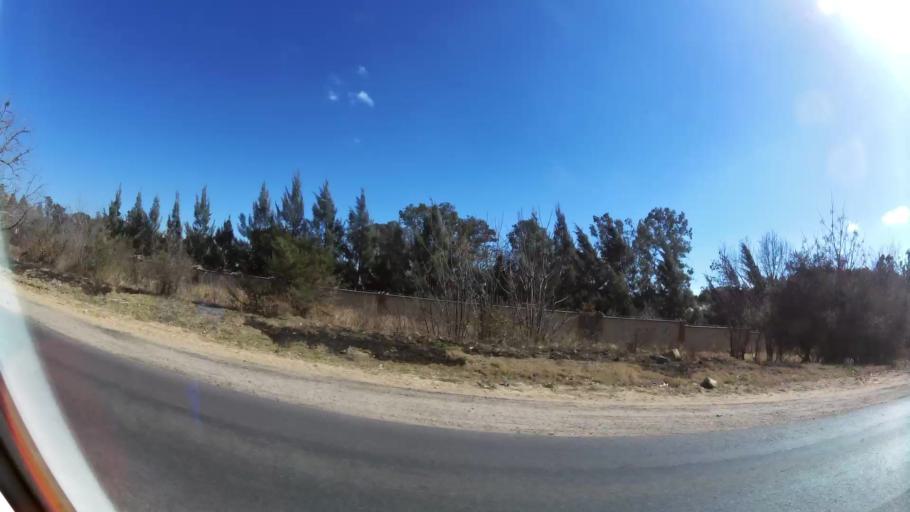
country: ZA
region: Gauteng
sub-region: City of Johannesburg Metropolitan Municipality
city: Midrand
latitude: -25.9615
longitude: 28.0823
